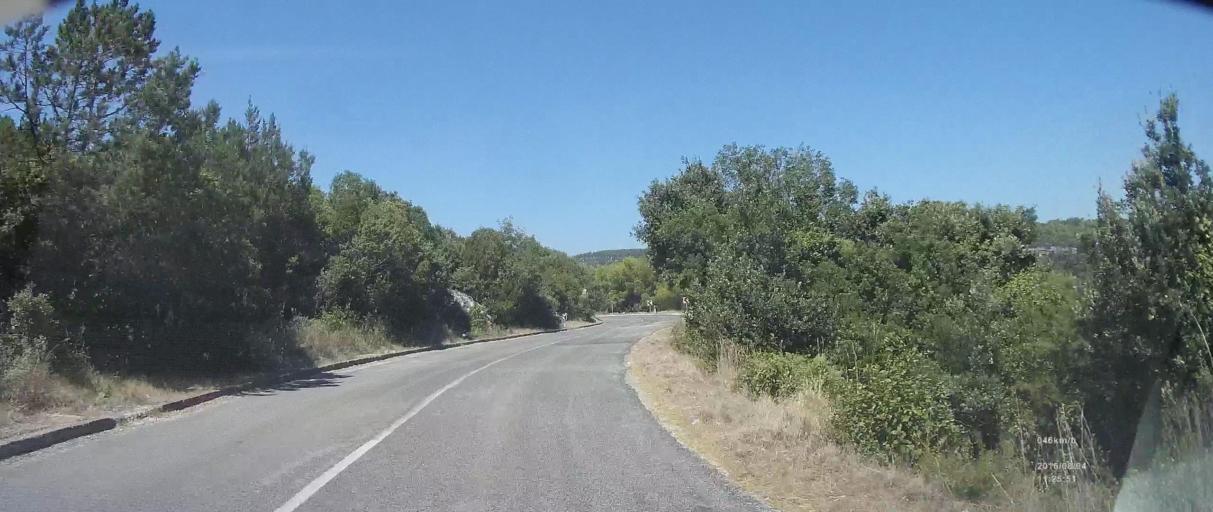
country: HR
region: Dubrovacko-Neretvanska
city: Blato
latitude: 42.7869
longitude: 17.3930
